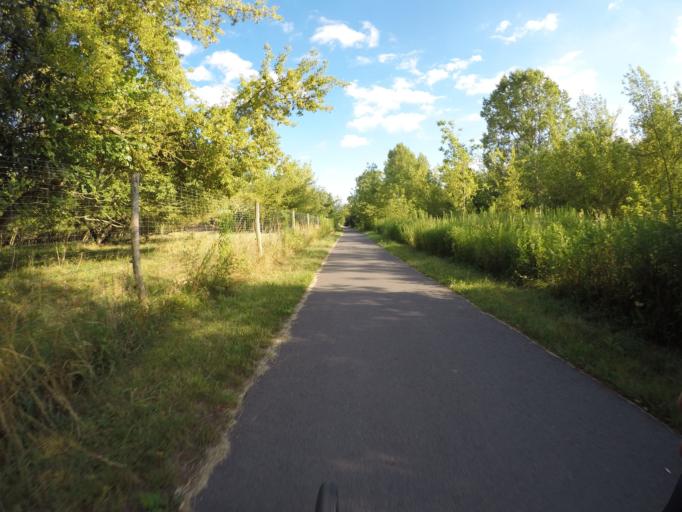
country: DE
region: Berlin
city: Stadtrandsiedlung Malchow
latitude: 52.5750
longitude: 13.4928
